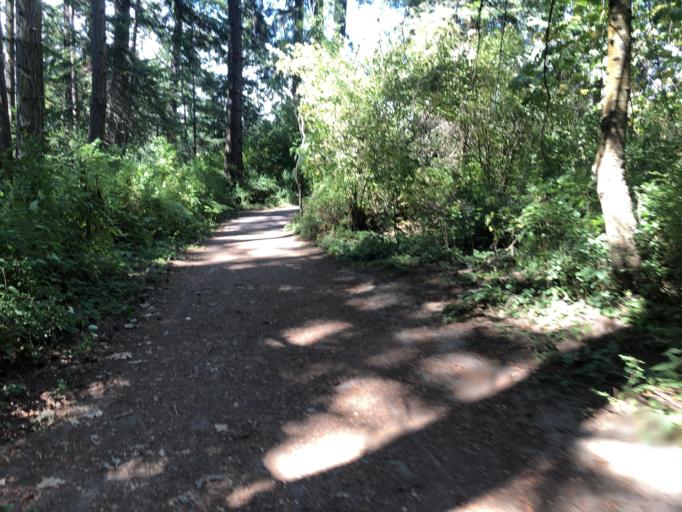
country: CA
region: British Columbia
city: Metchosin
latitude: 48.3652
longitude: -123.5409
